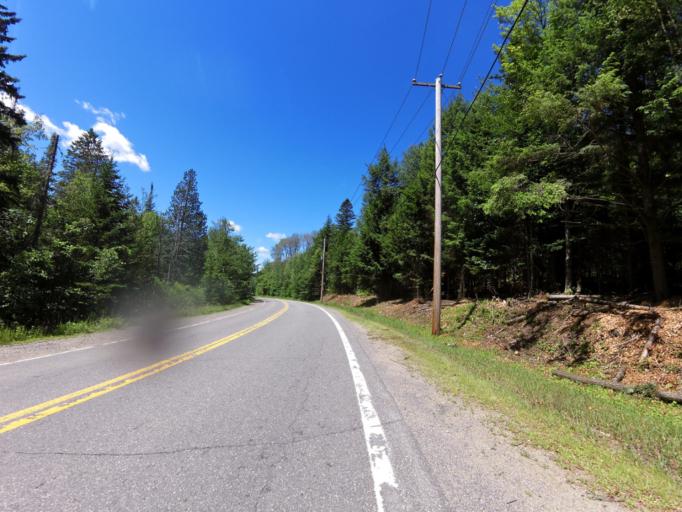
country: CA
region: Quebec
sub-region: Laurentides
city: Brownsburg-Chatham
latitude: 45.8510
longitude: -74.5621
